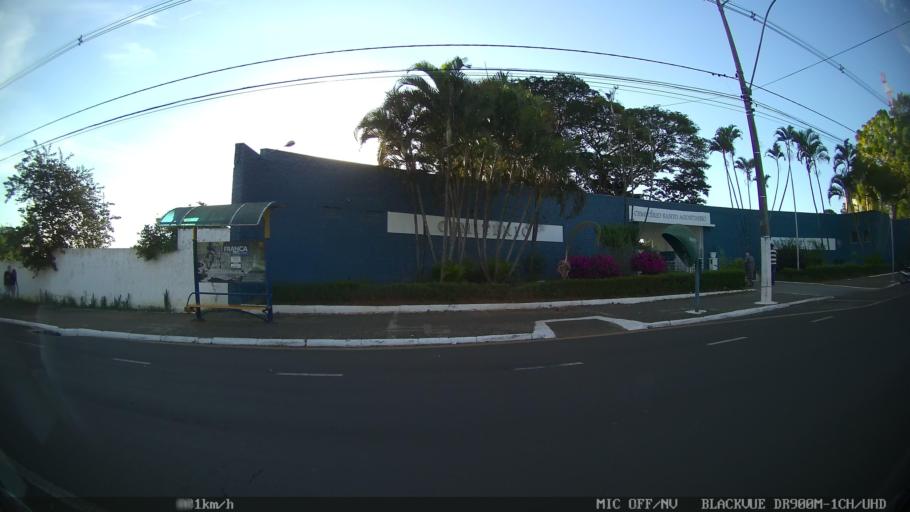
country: BR
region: Sao Paulo
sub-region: Franca
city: Franca
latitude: -20.5173
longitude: -47.3812
